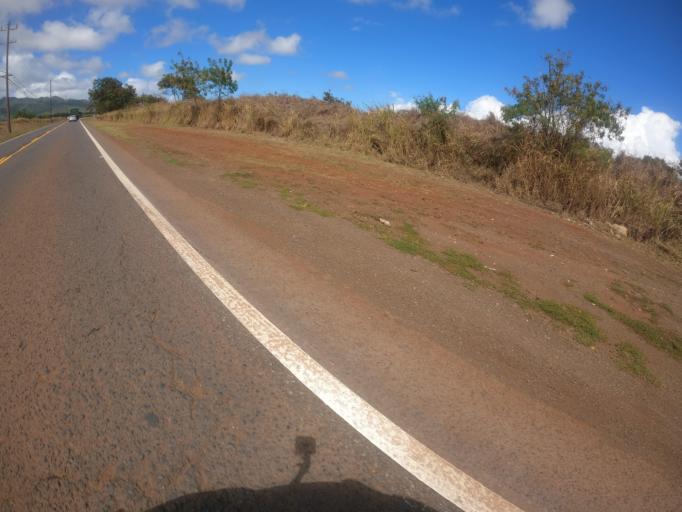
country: US
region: Hawaii
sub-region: Honolulu County
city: Village Park
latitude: 21.4253
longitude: -158.0536
